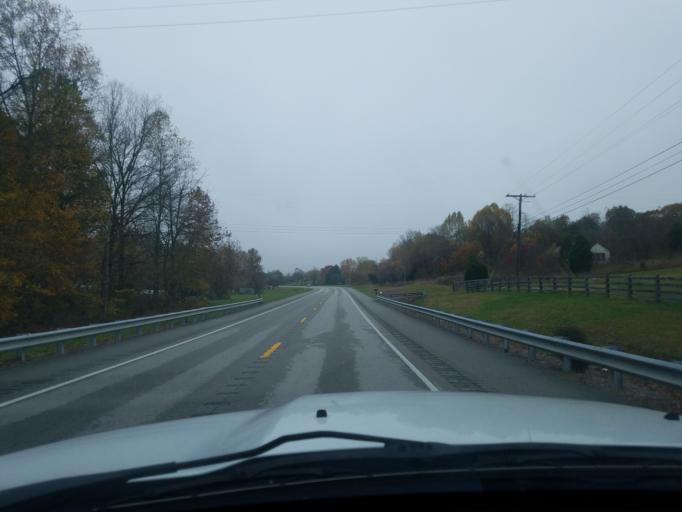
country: US
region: Kentucky
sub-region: Taylor County
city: Campbellsville
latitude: 37.3825
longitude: -85.4143
